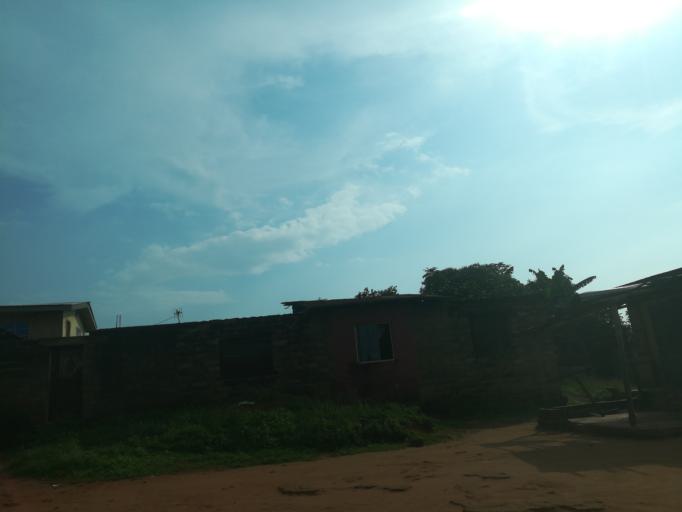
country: NG
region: Lagos
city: Ikorodu
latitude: 6.6629
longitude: 3.6699
